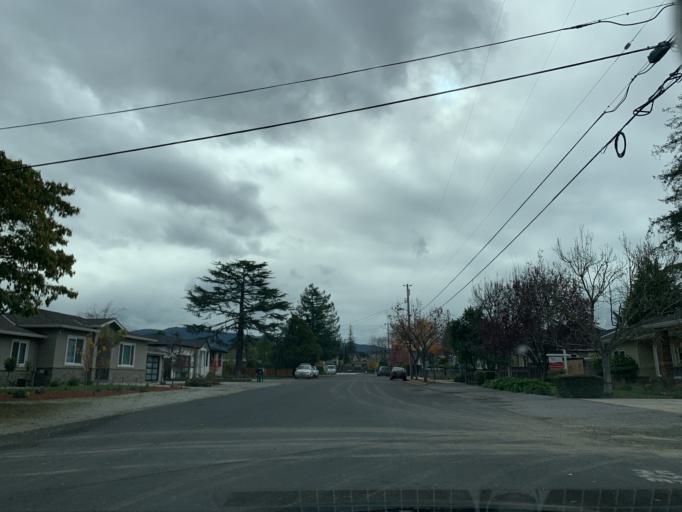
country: US
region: California
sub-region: Santa Clara County
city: Campbell
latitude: 37.2705
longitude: -121.9690
